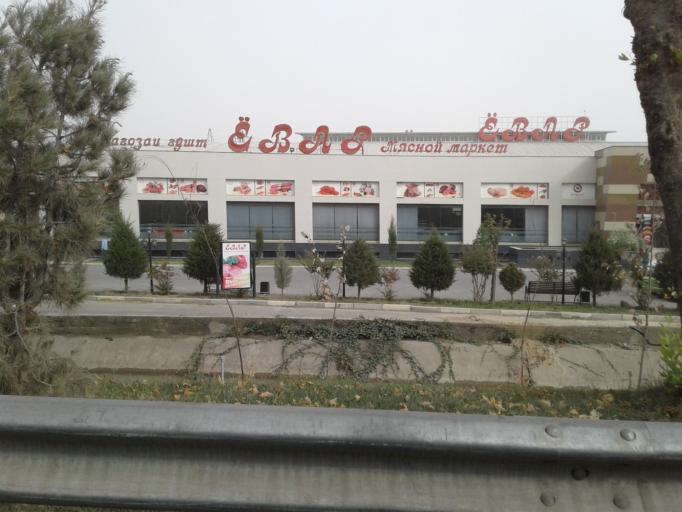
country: TJ
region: Dushanbe
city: Dushanbe
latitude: 38.5680
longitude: 68.7656
